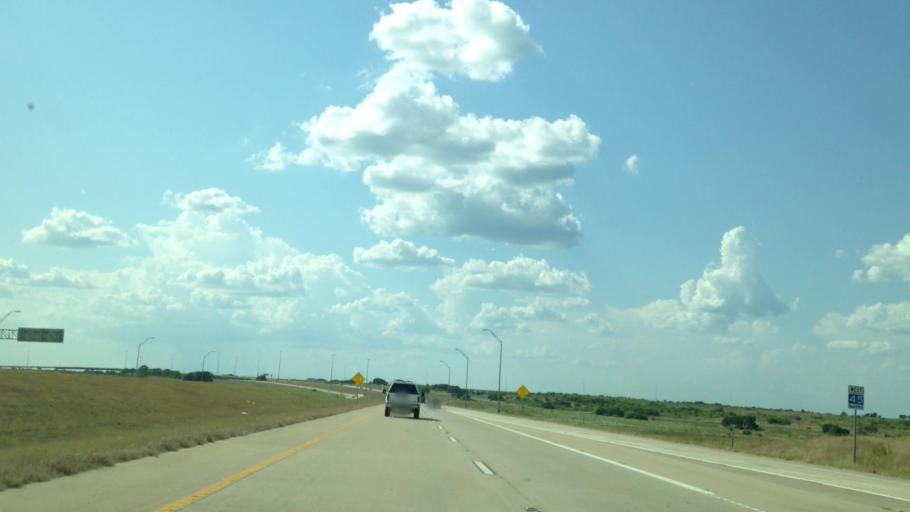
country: US
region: Texas
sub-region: Travis County
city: Onion Creek
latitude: 30.1046
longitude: -97.7857
